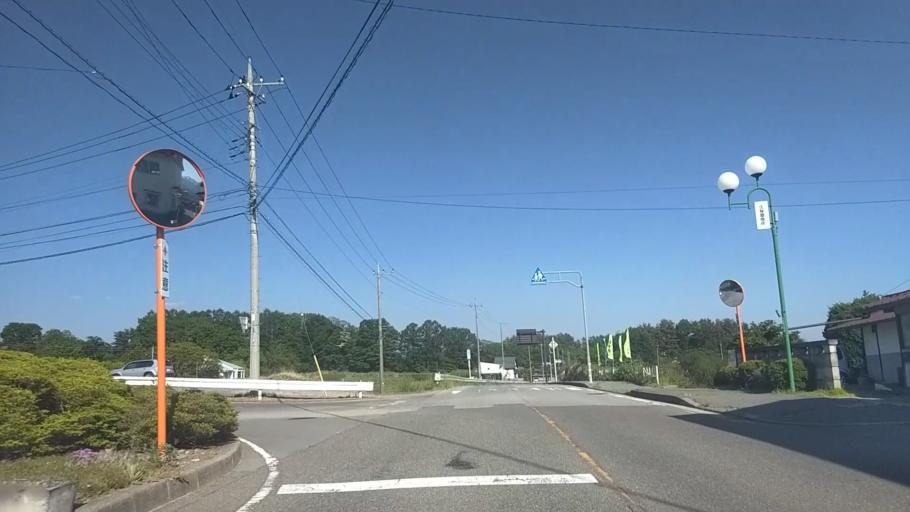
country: JP
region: Nagano
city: Chino
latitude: 35.8614
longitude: 138.3017
